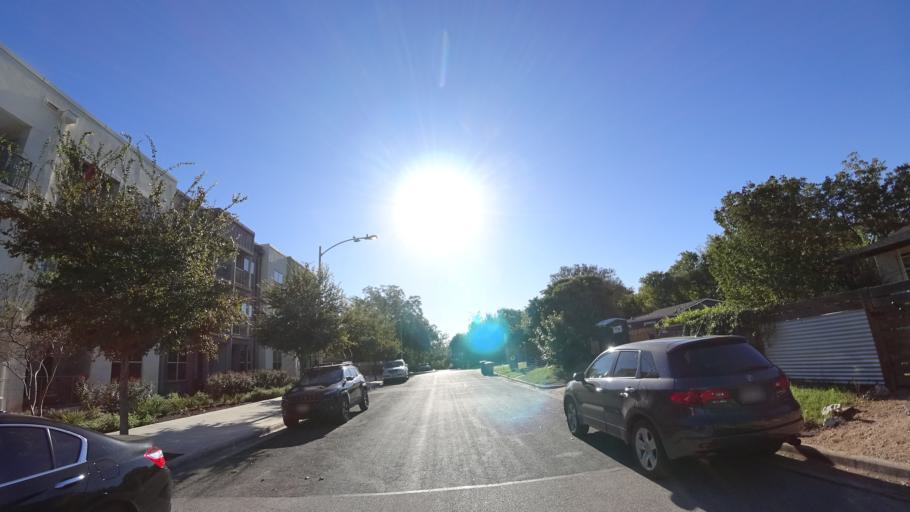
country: US
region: Texas
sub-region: Travis County
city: Austin
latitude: 30.2282
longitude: -97.7671
